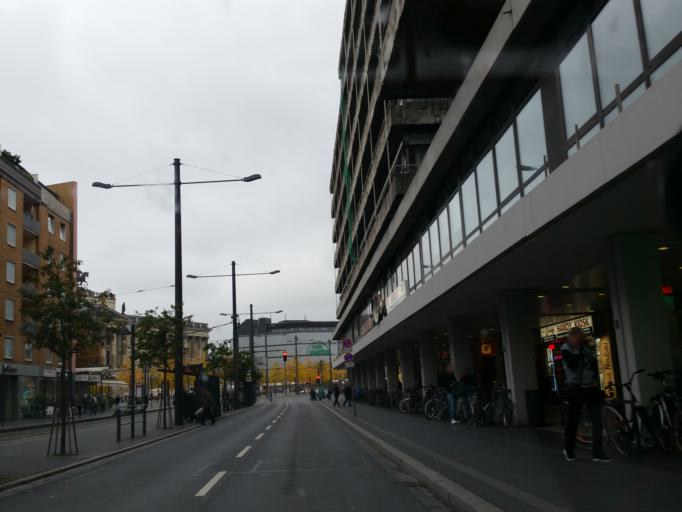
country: DE
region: Lower Saxony
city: Braunschweig
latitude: 52.2648
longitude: 10.5263
